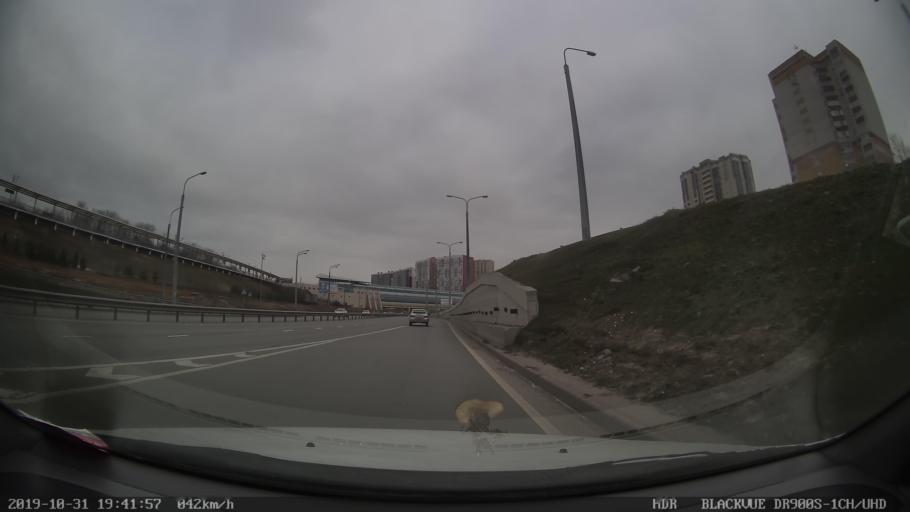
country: RU
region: Tatarstan
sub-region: Gorod Kazan'
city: Kazan
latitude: 55.7631
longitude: 49.1625
